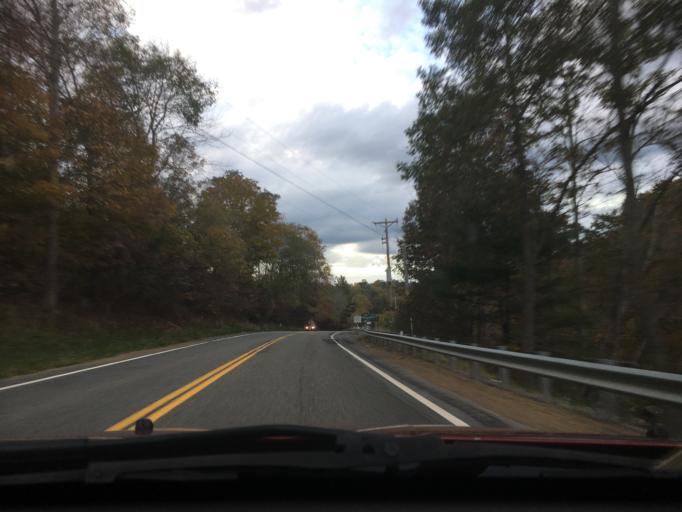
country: US
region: Virginia
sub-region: Pulaski County
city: Dublin
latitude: 37.2005
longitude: -80.7360
